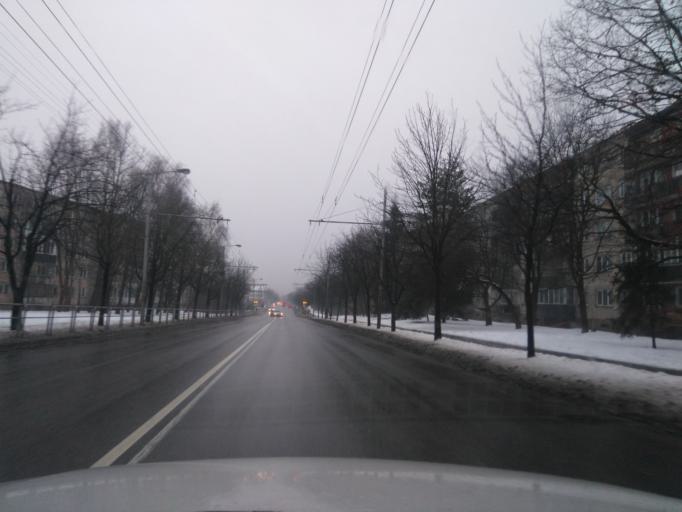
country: LT
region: Kauno apskritis
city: Dainava (Kaunas)
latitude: 54.9090
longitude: 23.9739
